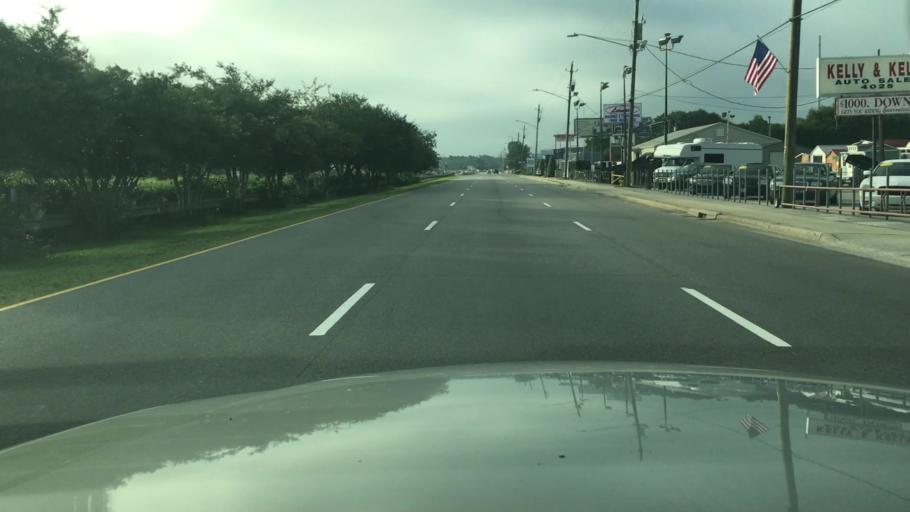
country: US
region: North Carolina
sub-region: Cumberland County
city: Fayetteville
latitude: 35.0827
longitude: -78.9458
